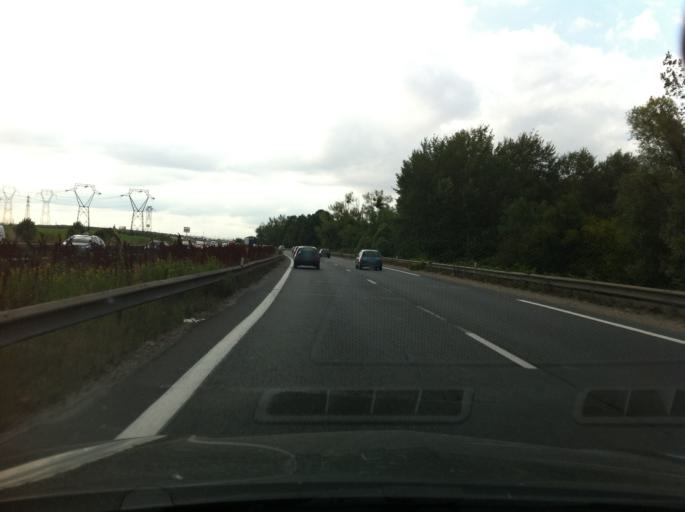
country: FR
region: Ile-de-France
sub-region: Departement de Seine-et-Marne
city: Villeparisis
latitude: 48.9537
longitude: 2.6279
